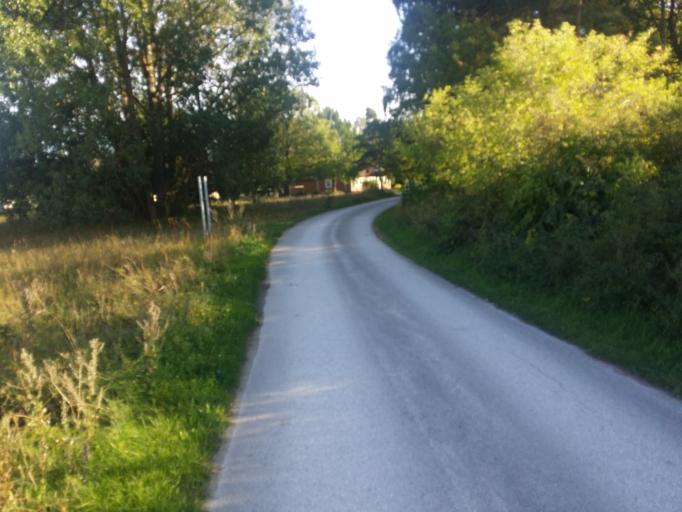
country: SE
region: Gotland
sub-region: Gotland
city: Klintehamn
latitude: 57.4845
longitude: 18.1378
